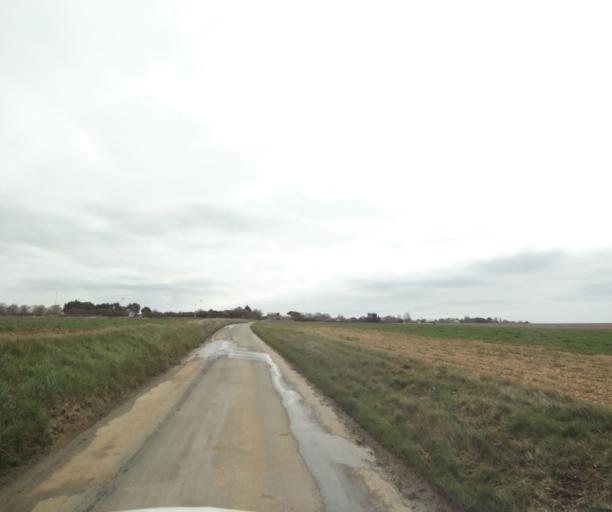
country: FR
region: Poitou-Charentes
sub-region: Departement de la Charente-Maritime
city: Nieul-sur-Mer
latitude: 46.1907
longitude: -1.1736
